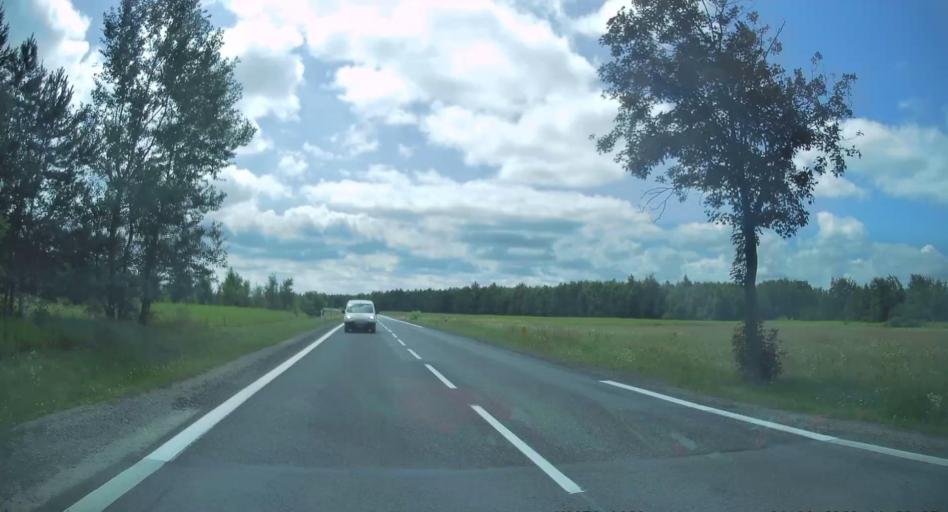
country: PL
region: Swietokrzyskie
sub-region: Powiat sandomierski
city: Klimontow
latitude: 50.6249
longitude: 21.4744
